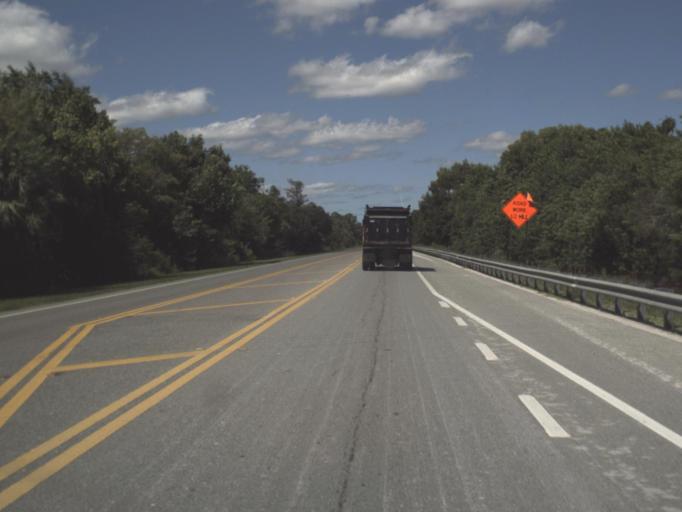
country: US
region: Florida
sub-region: Collier County
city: Lely Resort
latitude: 26.0263
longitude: -81.6412
